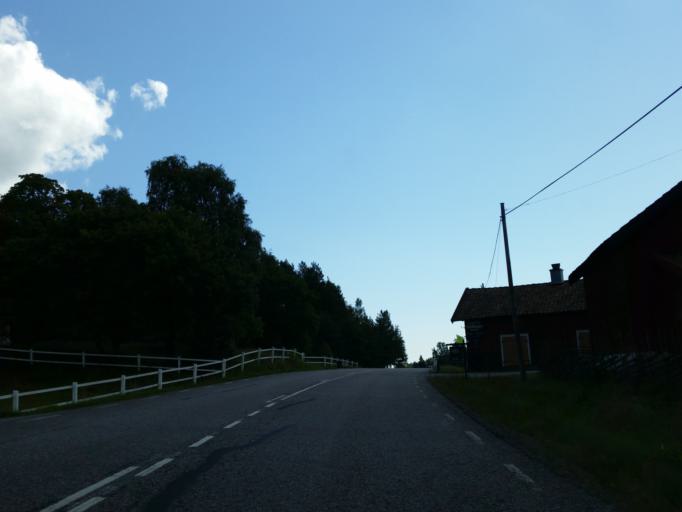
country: SE
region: Soedermanland
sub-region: Trosa Kommun
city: Vagnharad
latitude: 59.0018
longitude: 17.6027
